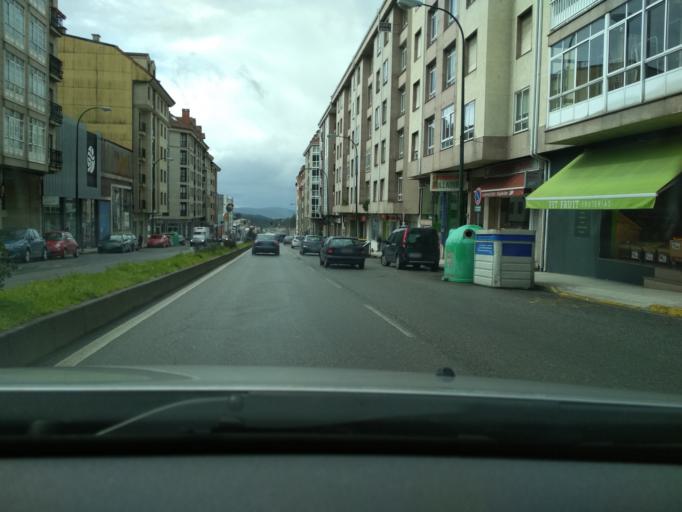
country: ES
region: Galicia
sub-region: Provincia da Coruna
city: Santiago de Compostela
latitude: 42.8419
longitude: -8.5791
